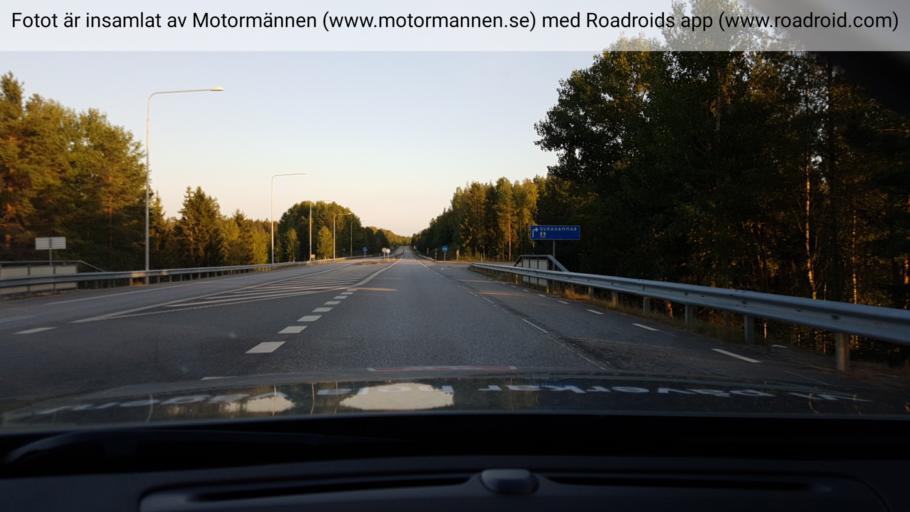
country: SE
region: Vaestmanland
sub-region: Surahammars Kommun
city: Surahammar
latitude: 59.7248
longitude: 16.2342
